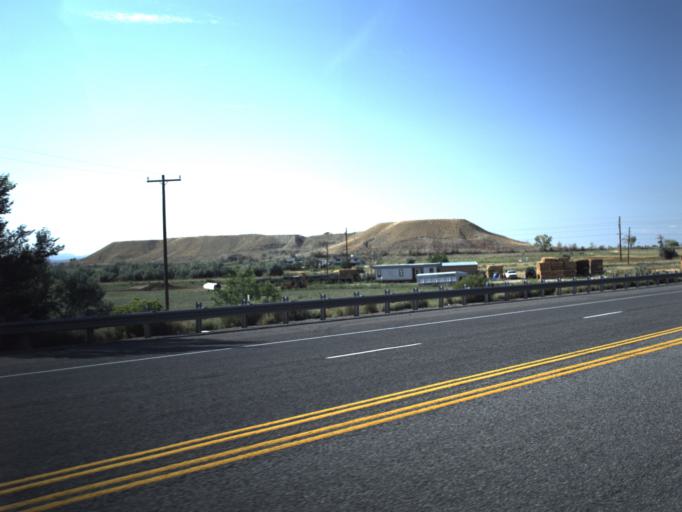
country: US
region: Utah
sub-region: Emery County
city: Huntington
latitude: 39.3475
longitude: -110.9368
